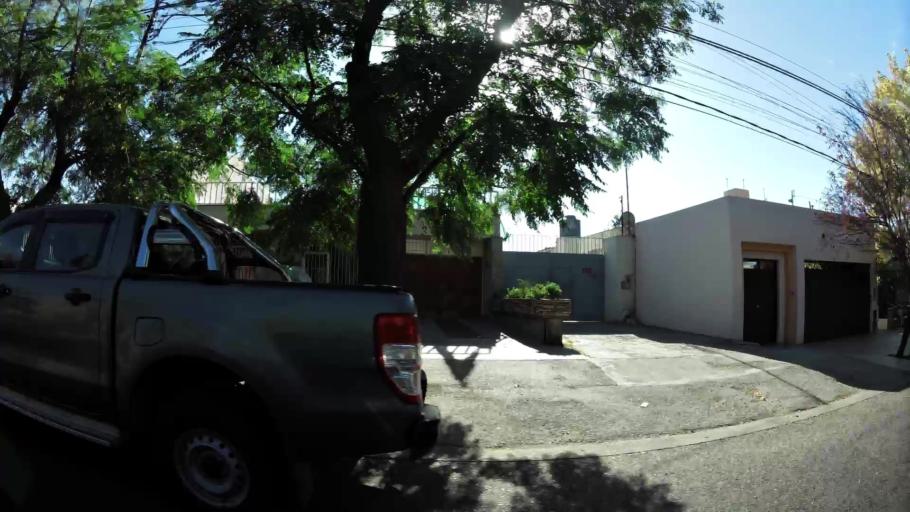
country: AR
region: Mendoza
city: Mendoza
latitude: -32.9014
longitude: -68.8173
